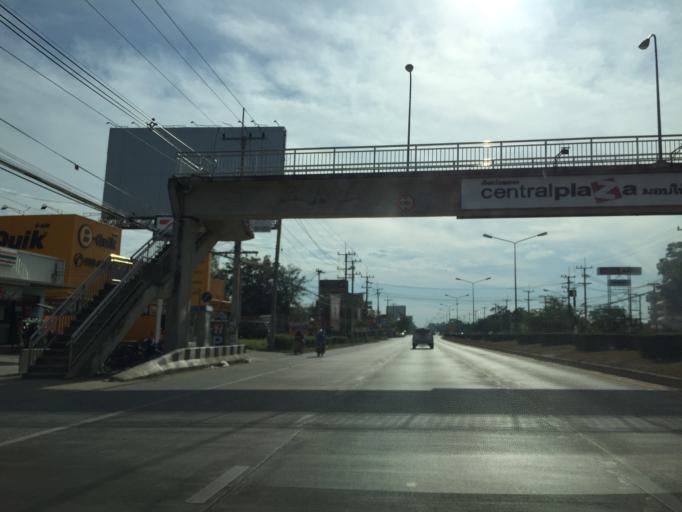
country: TH
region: Phitsanulok
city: Phitsanulok
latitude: 16.8413
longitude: 100.2339
